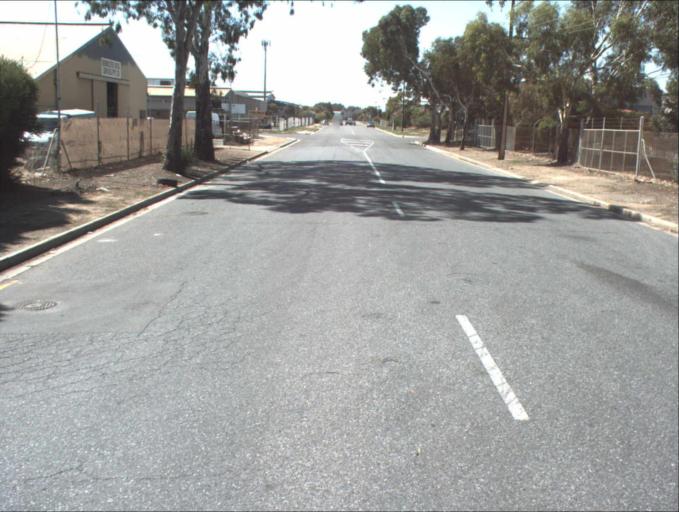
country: AU
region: South Australia
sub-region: Charles Sturt
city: Woodville North
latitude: -34.8462
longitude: 138.5598
